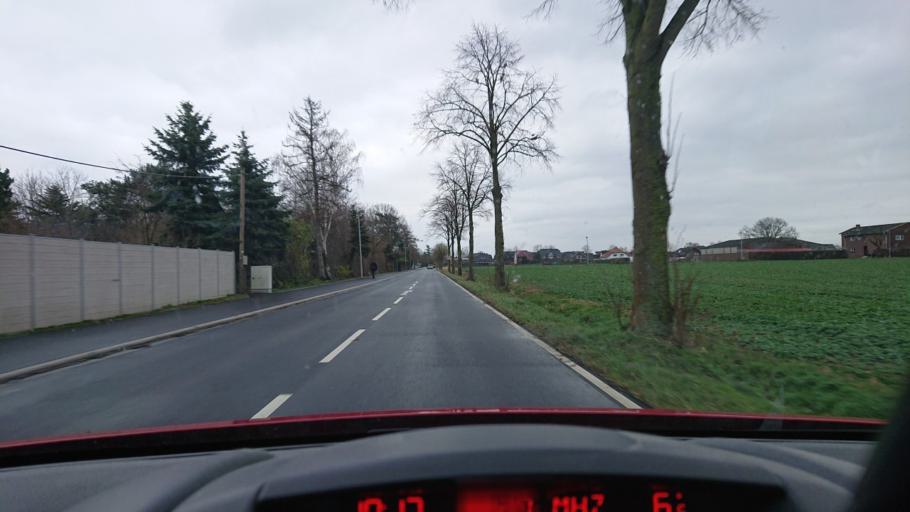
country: DE
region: North Rhine-Westphalia
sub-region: Regierungsbezirk Koln
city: Bergheim
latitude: 50.9137
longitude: 6.6260
